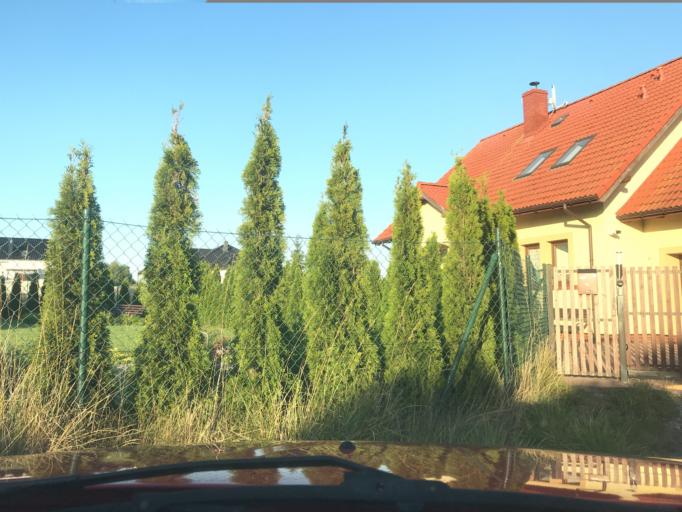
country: PL
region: Greater Poland Voivodeship
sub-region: Powiat poznanski
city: Tarnowo Podgorne
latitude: 52.4396
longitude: 16.7123
